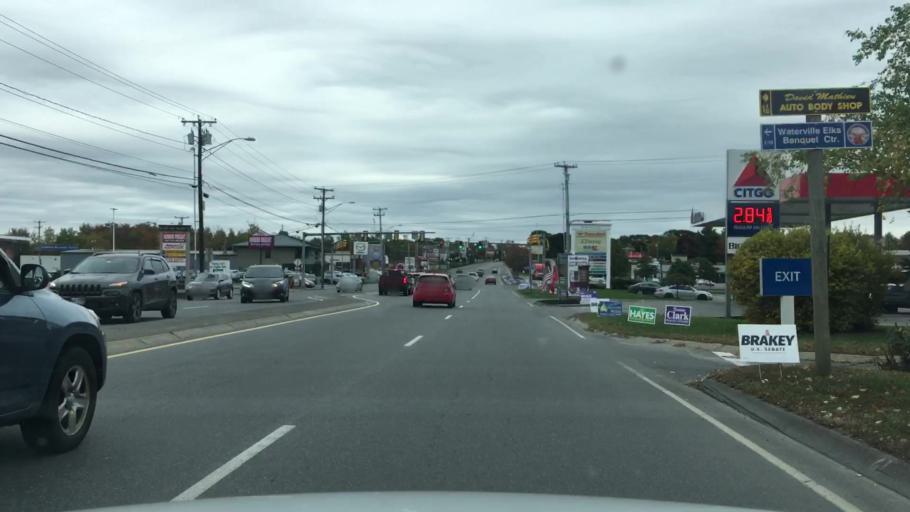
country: US
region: Maine
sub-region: Kennebec County
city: Waterville
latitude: 44.5698
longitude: -69.6397
